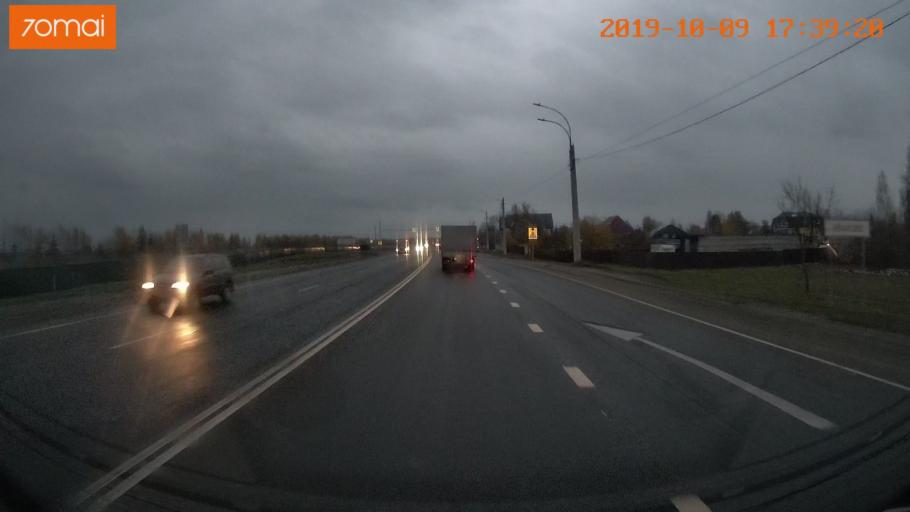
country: RU
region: Ivanovo
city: Bogorodskoye
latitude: 57.0615
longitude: 40.9572
